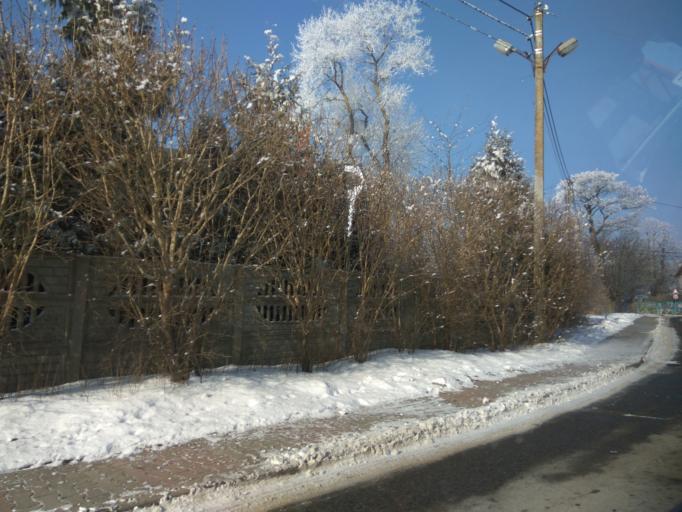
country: RU
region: Kaliningrad
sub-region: Zelenogradskiy Rayon
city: Zelenogradsk
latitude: 55.0143
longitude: 20.6187
